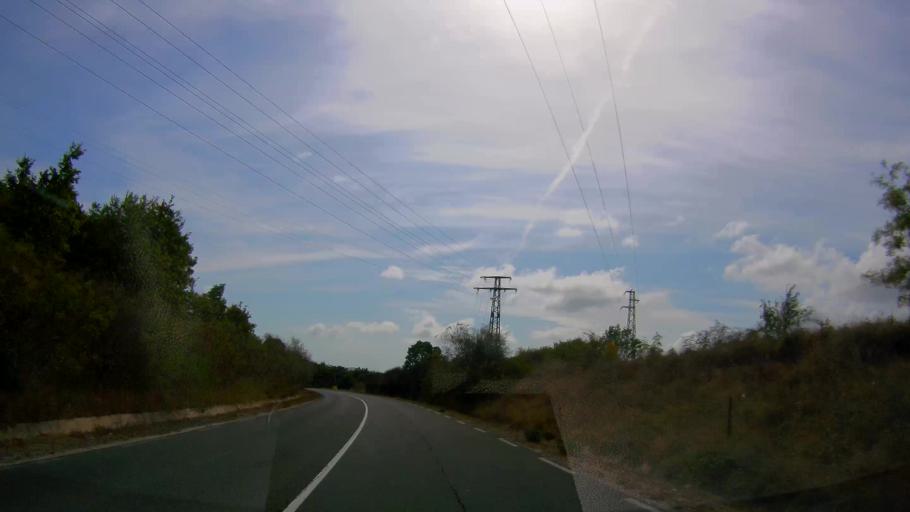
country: BG
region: Burgas
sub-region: Obshtina Sozopol
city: Sozopol
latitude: 42.3694
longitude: 27.6843
